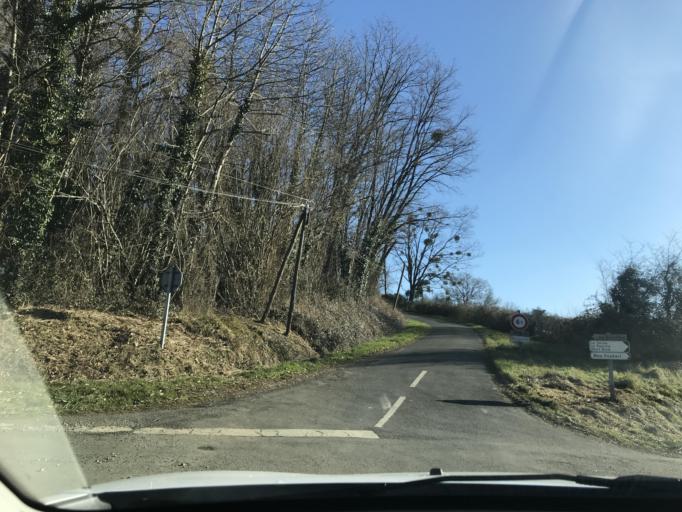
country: FR
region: Poitou-Charentes
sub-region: Departement de la Charente
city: Chasseneuil-sur-Bonnieure
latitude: 45.8458
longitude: 0.5114
